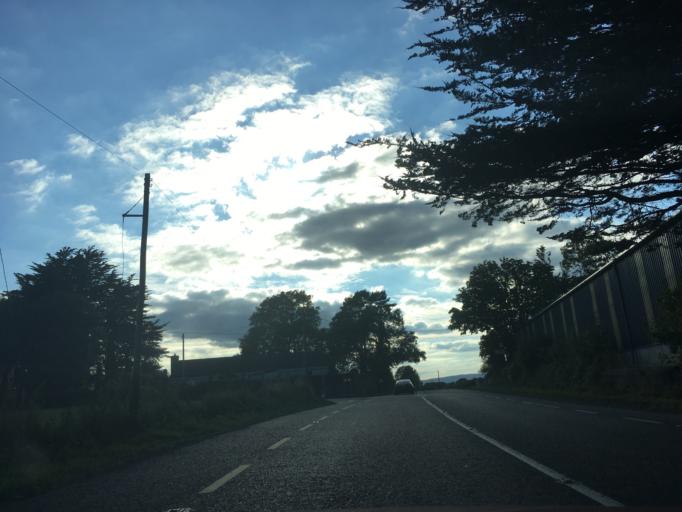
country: IE
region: Leinster
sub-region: Kilkenny
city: Mooncoin
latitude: 52.2819
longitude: -7.2013
